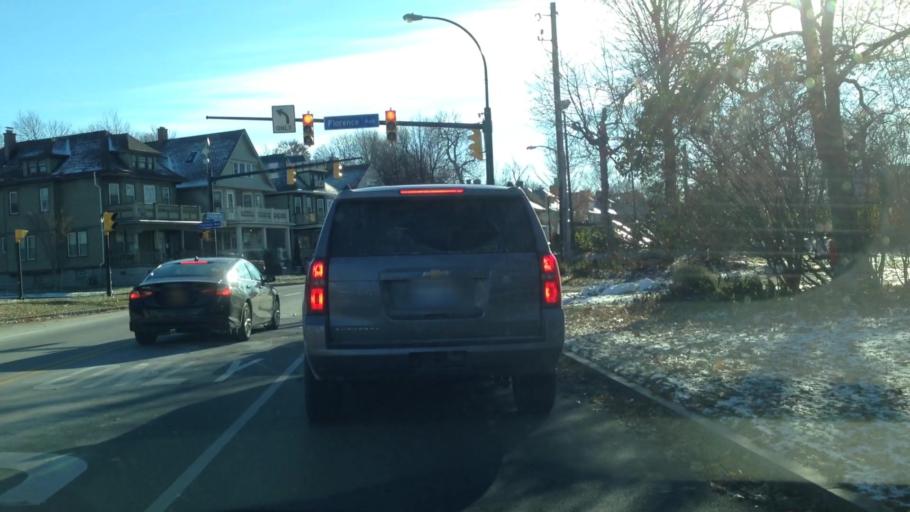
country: US
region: New York
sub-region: Erie County
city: Kenmore
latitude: 42.9334
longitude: -78.8519
